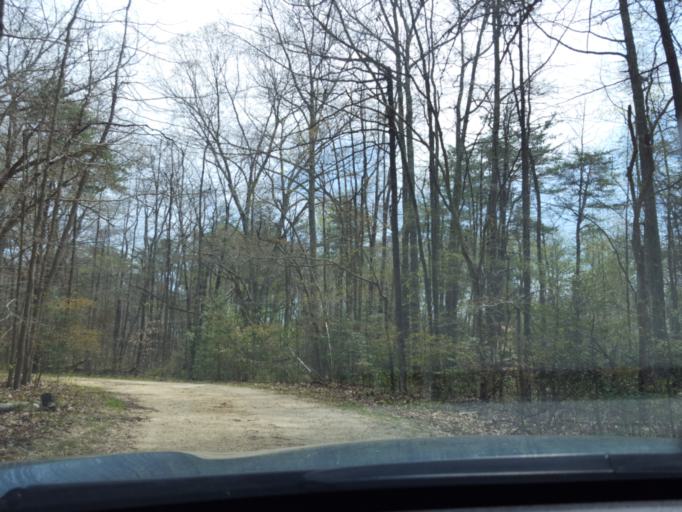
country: US
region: Maryland
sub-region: Calvert County
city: Dunkirk
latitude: 38.7414
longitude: -76.7058
